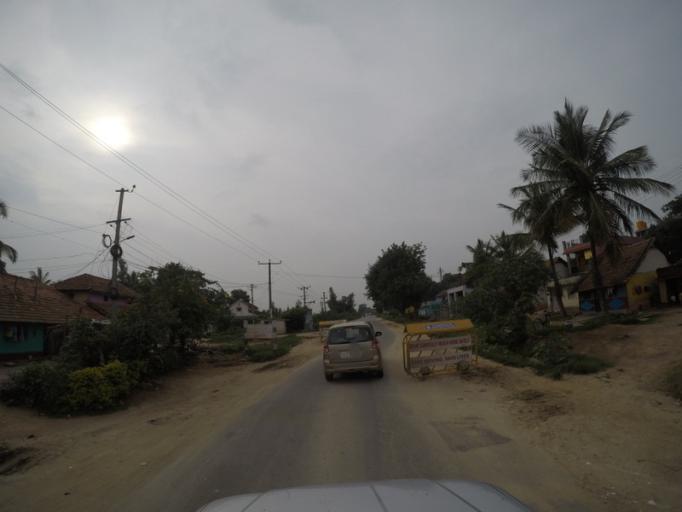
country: IN
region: Karnataka
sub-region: Chikmagalur
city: Chikmagalur
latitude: 13.2667
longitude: 75.8366
